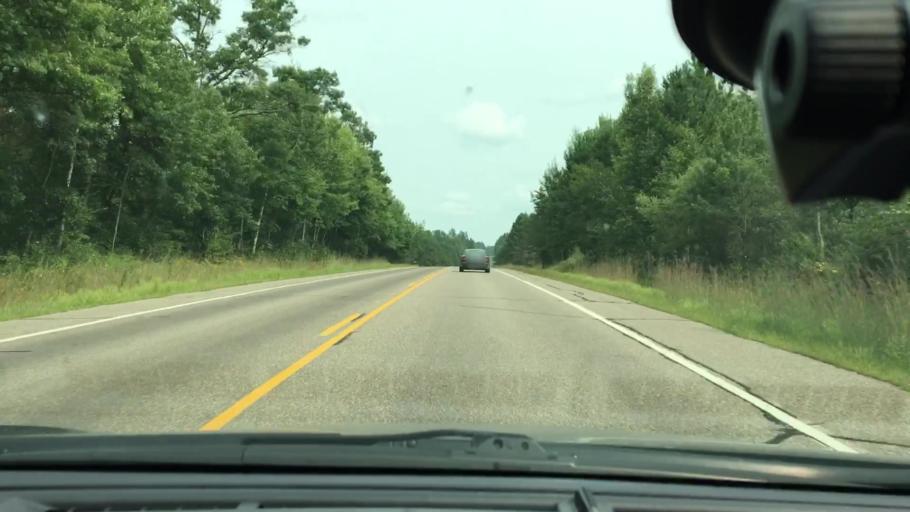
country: US
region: Minnesota
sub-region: Crow Wing County
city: Cross Lake
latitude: 46.7308
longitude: -93.9905
